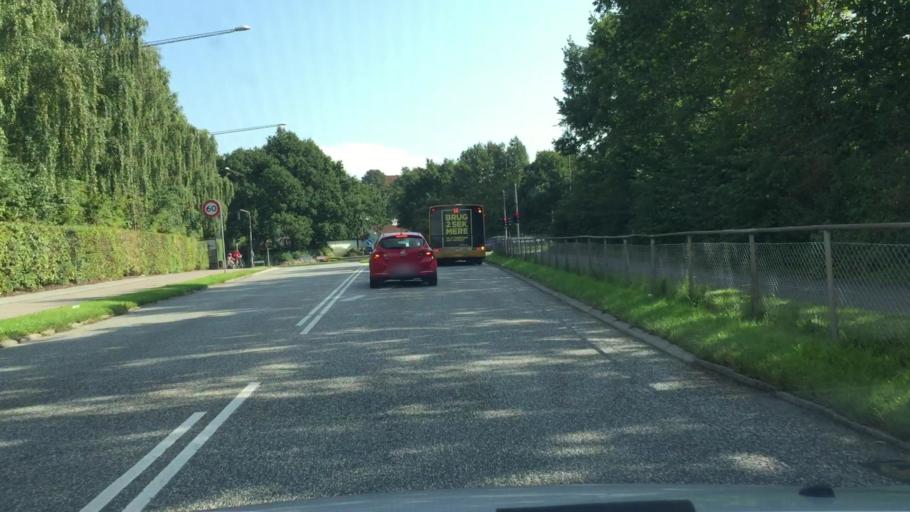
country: DK
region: Central Jutland
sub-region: Arhus Kommune
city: Arhus
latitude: 56.1964
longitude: 10.2080
